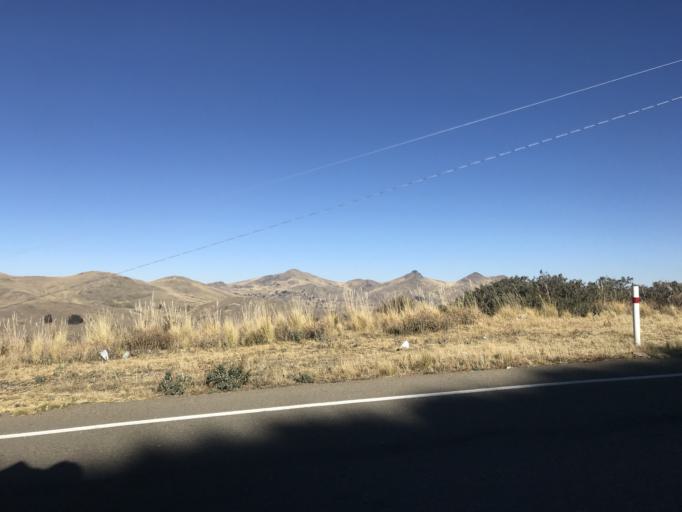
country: PE
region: Puno
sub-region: Yunguyo
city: Yunguyo
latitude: -16.1801
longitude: -68.9825
